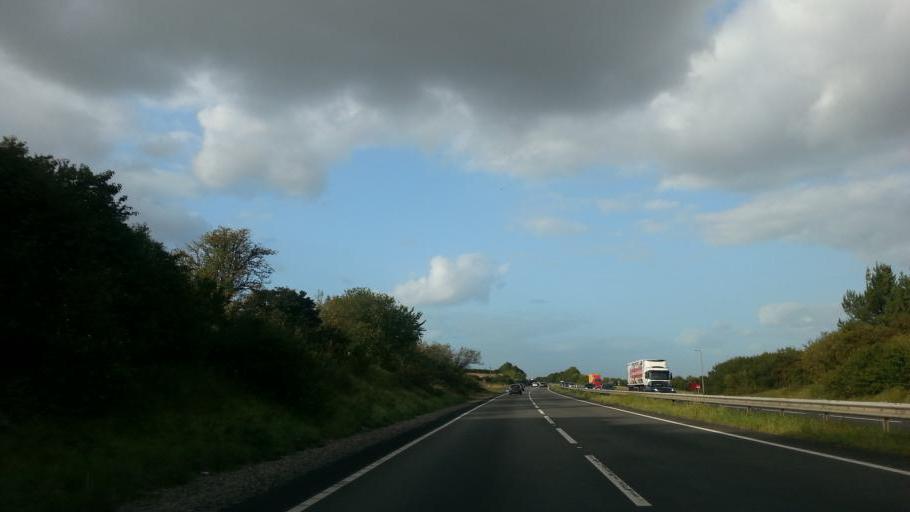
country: GB
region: England
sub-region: Hampshire
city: Kings Worthy
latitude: 51.1569
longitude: -1.3453
